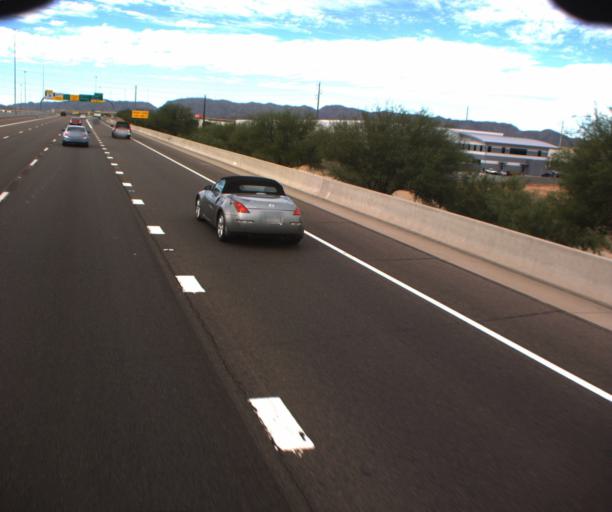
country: US
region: Arizona
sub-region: Maricopa County
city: Guadalupe
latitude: 33.2946
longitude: -111.9577
